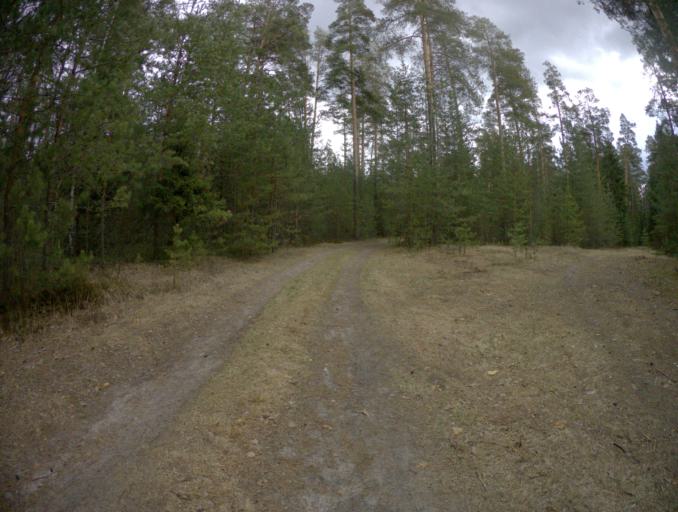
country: RU
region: Vladimir
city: Raduzhnyy
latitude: 55.9494
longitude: 40.2567
